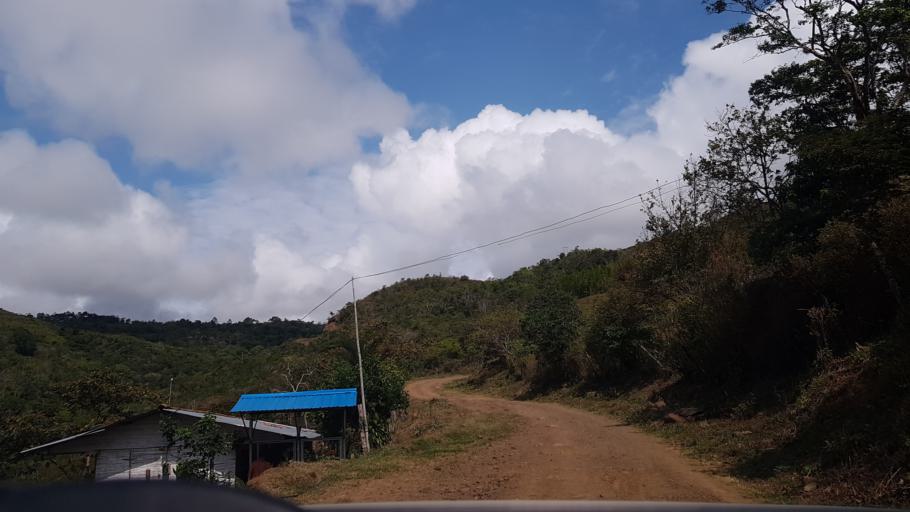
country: CO
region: Valle del Cauca
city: Yumbo
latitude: 3.6523
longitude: -76.5148
